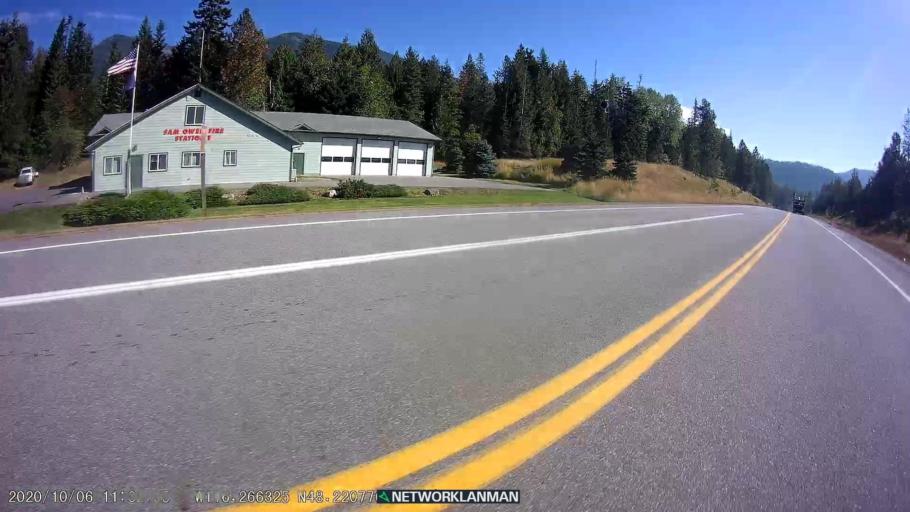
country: US
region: Idaho
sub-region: Bonner County
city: Ponderay
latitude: 48.2205
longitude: -116.2658
